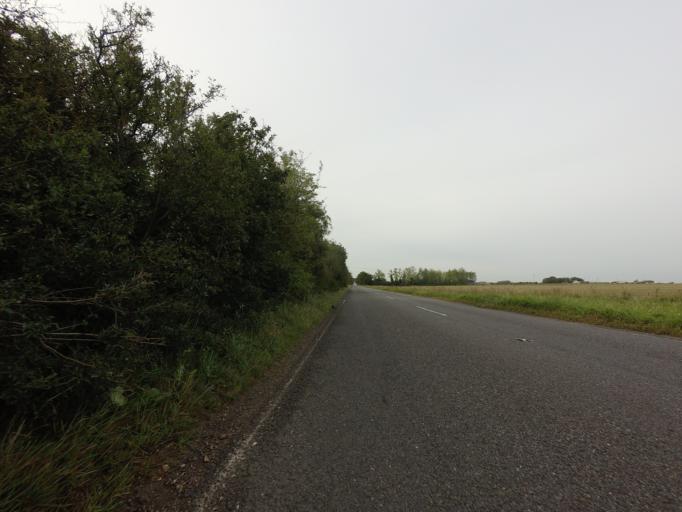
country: GB
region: England
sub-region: Cambridgeshire
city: Melbourn
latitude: 52.0700
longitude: 0.0580
